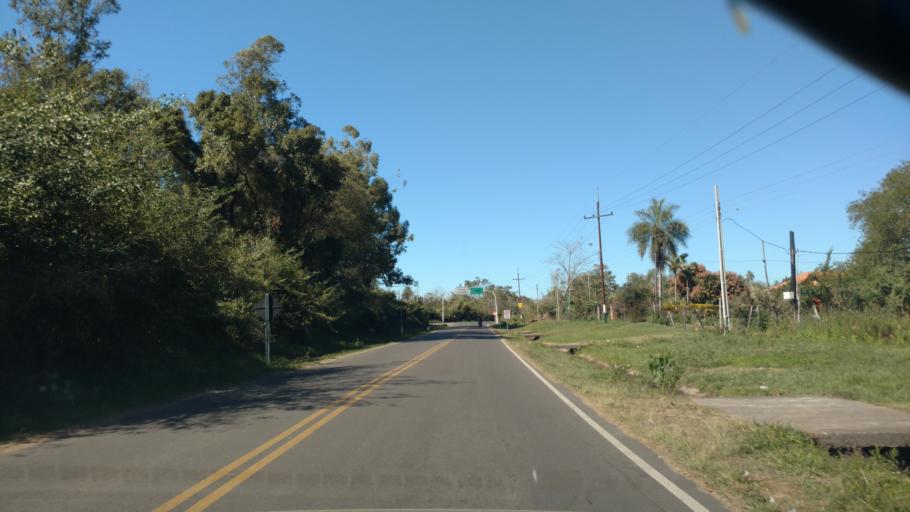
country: PY
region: Central
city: Ypacarai
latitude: -25.4390
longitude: -57.2782
